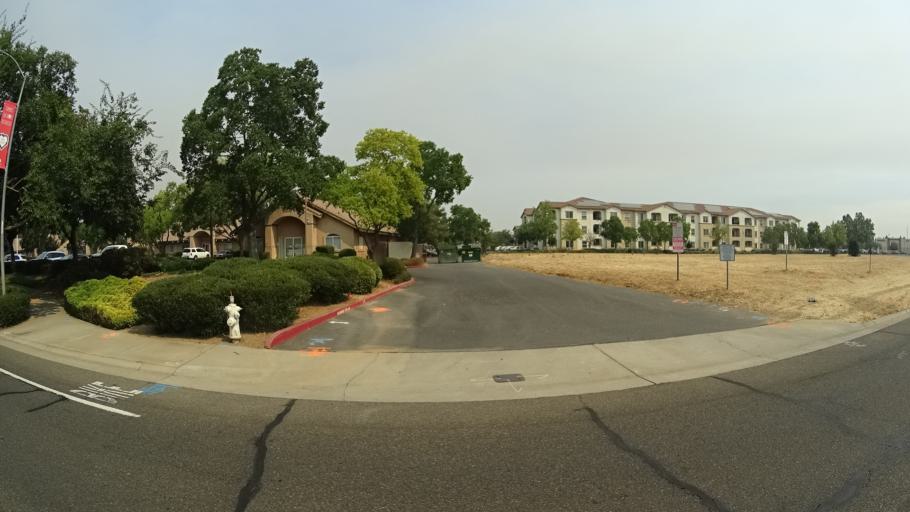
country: US
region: California
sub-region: Sacramento County
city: Laguna
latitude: 38.4220
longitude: -121.4079
